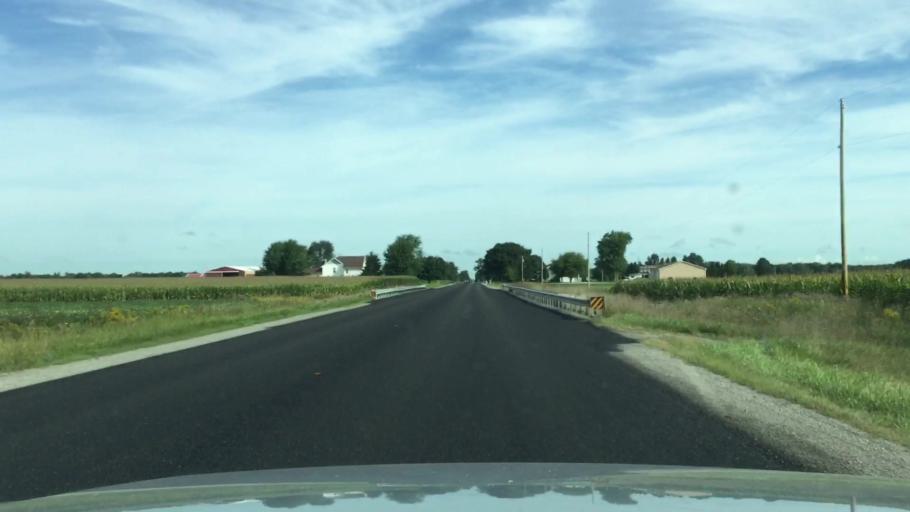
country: US
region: Michigan
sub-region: Genesee County
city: Montrose
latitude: 43.1347
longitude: -83.9292
